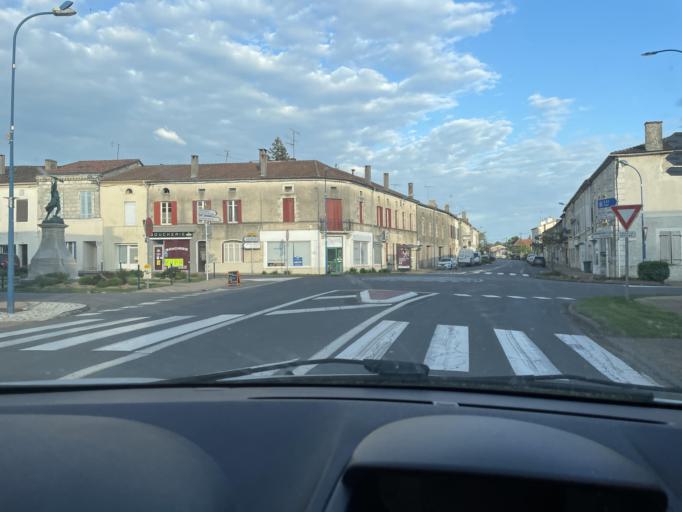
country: FR
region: Aquitaine
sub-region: Departement de la Gironde
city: Grignols
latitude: 44.3875
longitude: -0.0446
